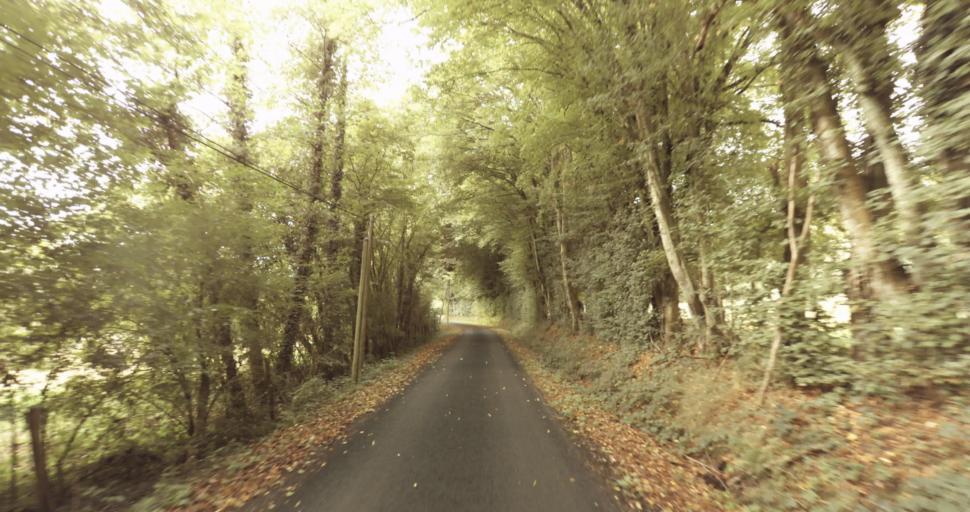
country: FR
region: Lower Normandy
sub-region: Departement de l'Orne
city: Gace
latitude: 48.8502
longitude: 0.2839
